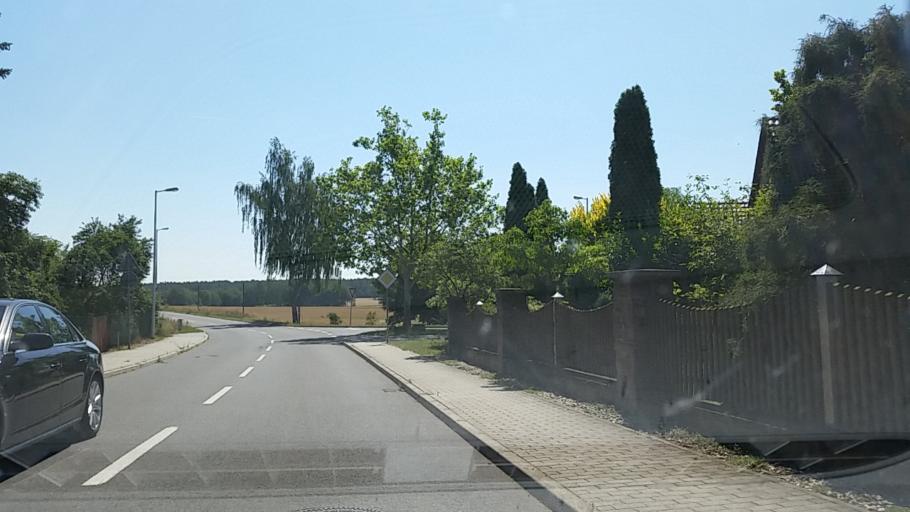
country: DE
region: Saxony-Anhalt
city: Bad Schmiedeberg
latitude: 51.6873
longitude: 12.7574
